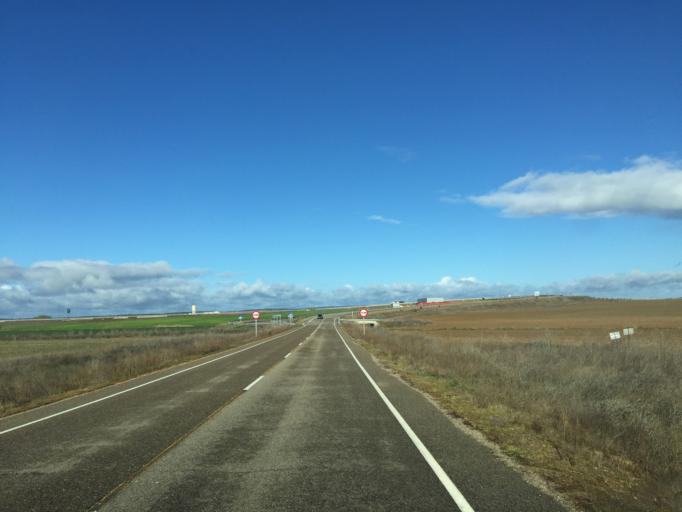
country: ES
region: Castille and Leon
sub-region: Provincia de Zamora
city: Manganeses de la Lampreana
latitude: 41.7603
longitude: -5.7474
